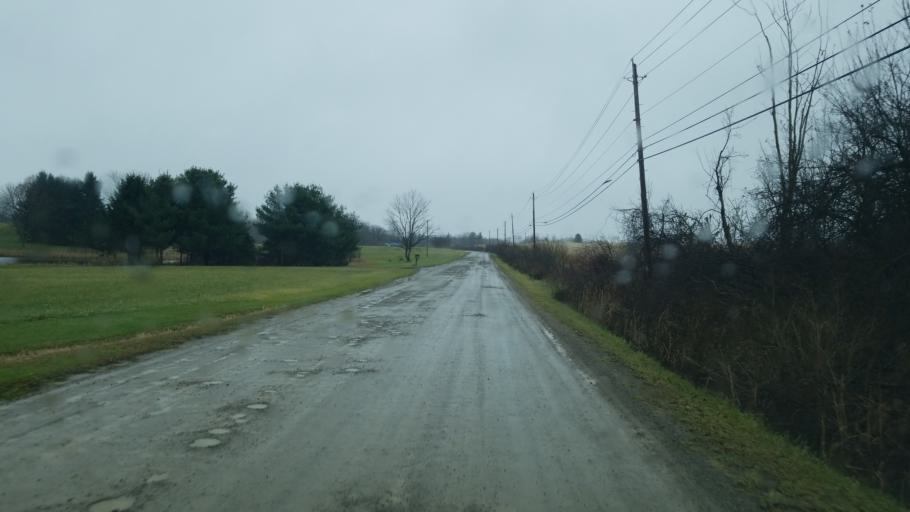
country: US
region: Ohio
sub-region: Ashtabula County
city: Conneaut
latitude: 41.9000
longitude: -80.5800
